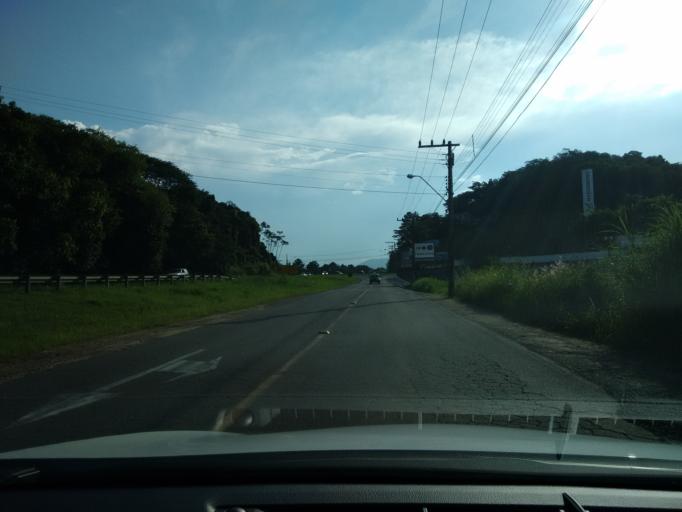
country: BR
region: Santa Catarina
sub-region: Blumenau
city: Blumenau
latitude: -26.8638
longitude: -49.0981
